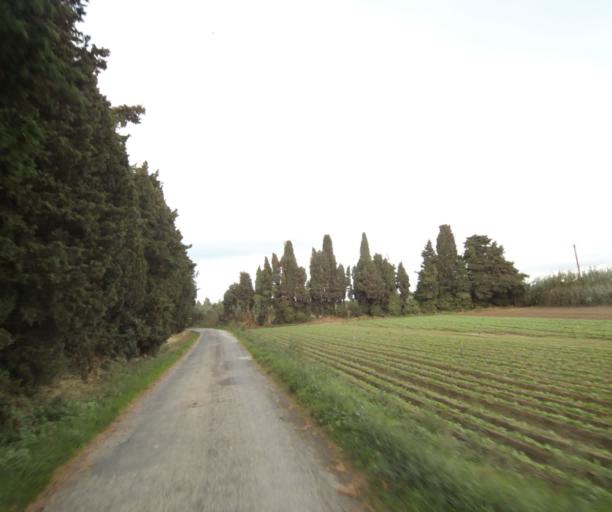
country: FR
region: Languedoc-Roussillon
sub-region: Departement des Pyrenees-Orientales
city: Latour-Bas-Elne
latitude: 42.5854
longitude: 3.0140
